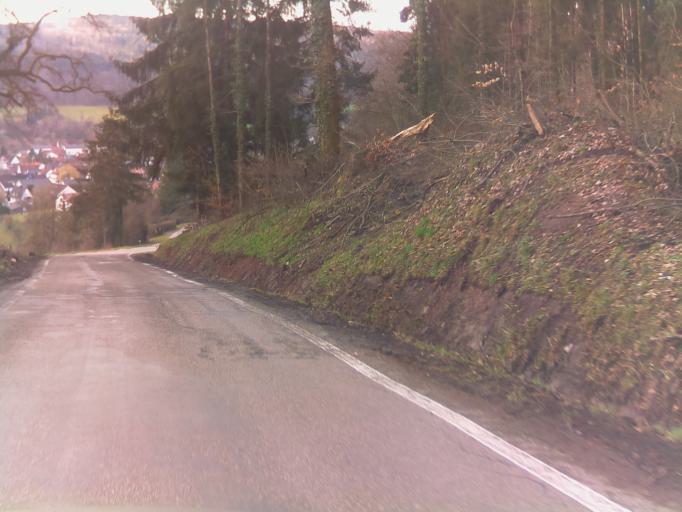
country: DE
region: Baden-Wuerttemberg
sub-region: Regierungsbezirk Stuttgart
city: Sulzbach an der Murr
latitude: 49.0129
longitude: 9.4968
